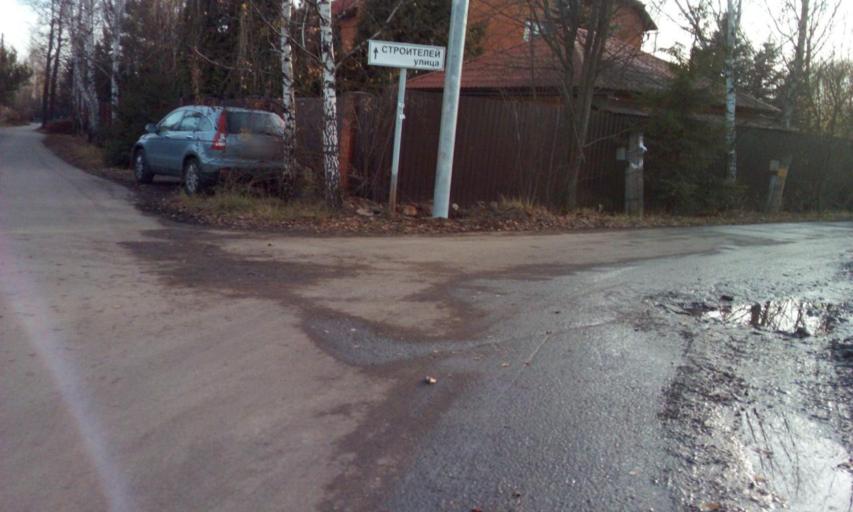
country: RU
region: Moskovskaya
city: Aprelevka
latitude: 55.5776
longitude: 37.1117
